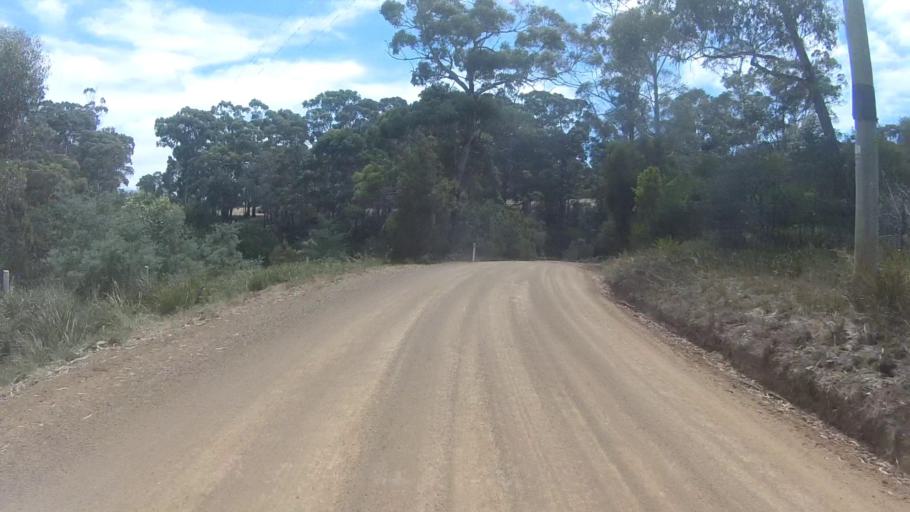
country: AU
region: Tasmania
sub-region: Kingborough
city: Blackmans Bay
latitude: -43.0471
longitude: 147.3075
